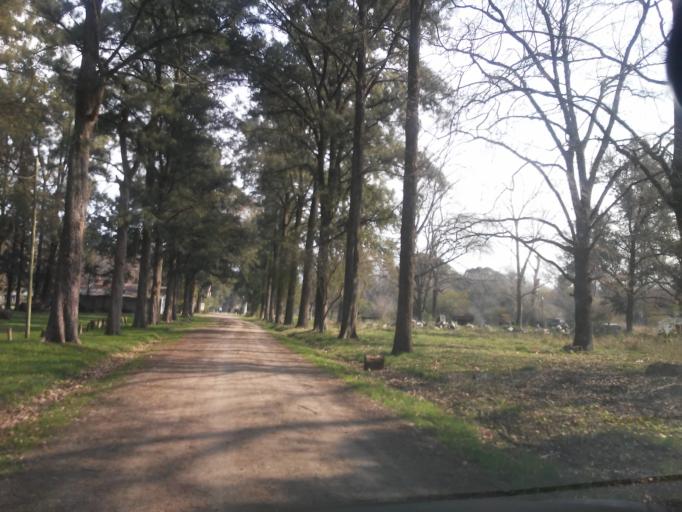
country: AR
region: Buenos Aires
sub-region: Partido de General Rodriguez
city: General Rodriguez
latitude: -34.6643
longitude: -58.8595
